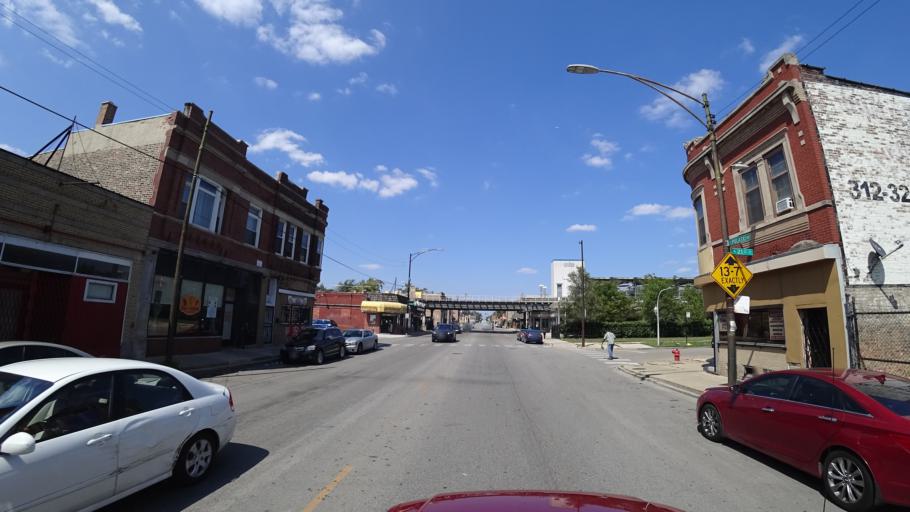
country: US
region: Illinois
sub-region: Cook County
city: Cicero
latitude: 41.8532
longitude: -87.7248
